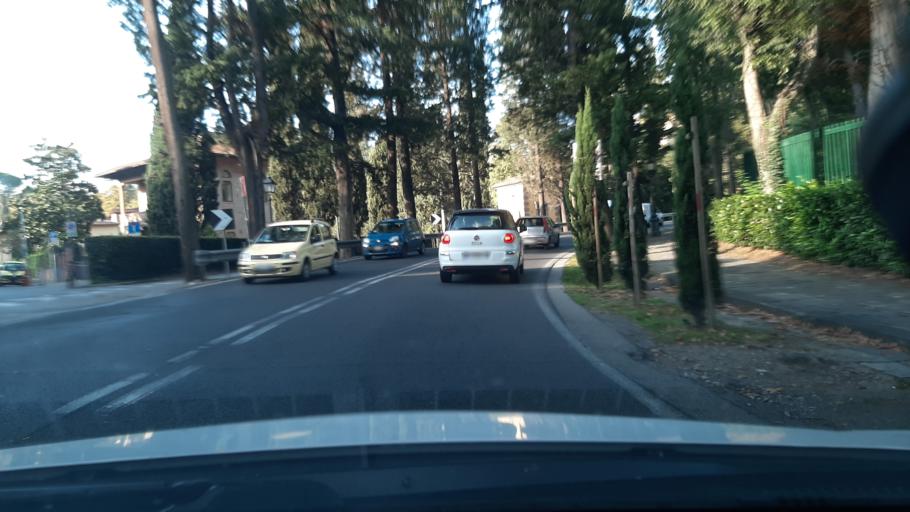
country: IT
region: Tuscany
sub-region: Province of Florence
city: Florence
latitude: 43.7565
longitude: 11.2698
